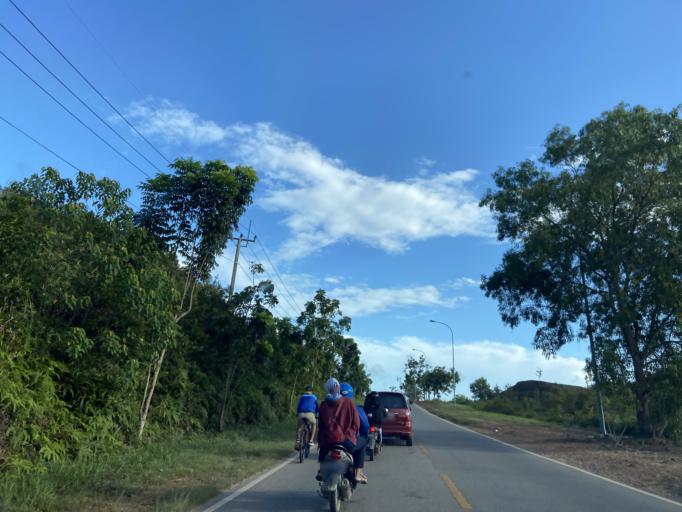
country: SG
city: Singapore
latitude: 0.9891
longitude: 104.0364
